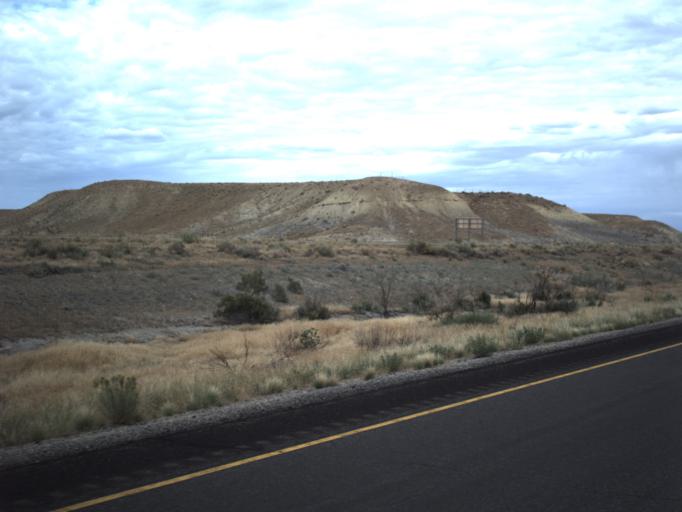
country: US
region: Utah
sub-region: Grand County
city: Moab
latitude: 38.9427
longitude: -109.6360
